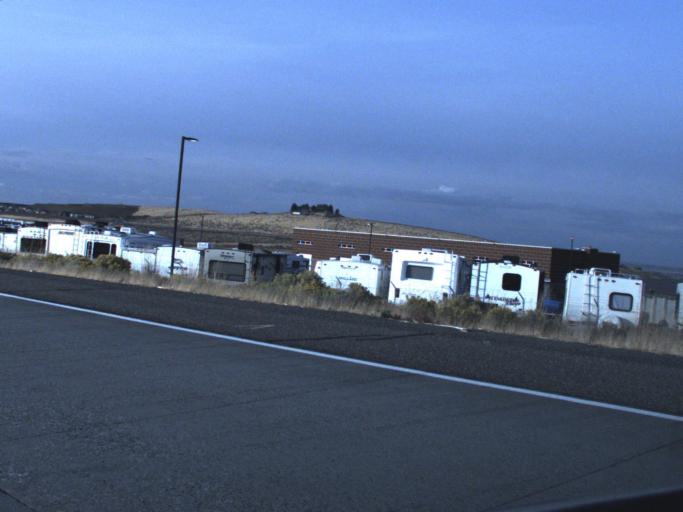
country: US
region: Washington
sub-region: Franklin County
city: West Pasco
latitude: 46.1701
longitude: -119.2059
